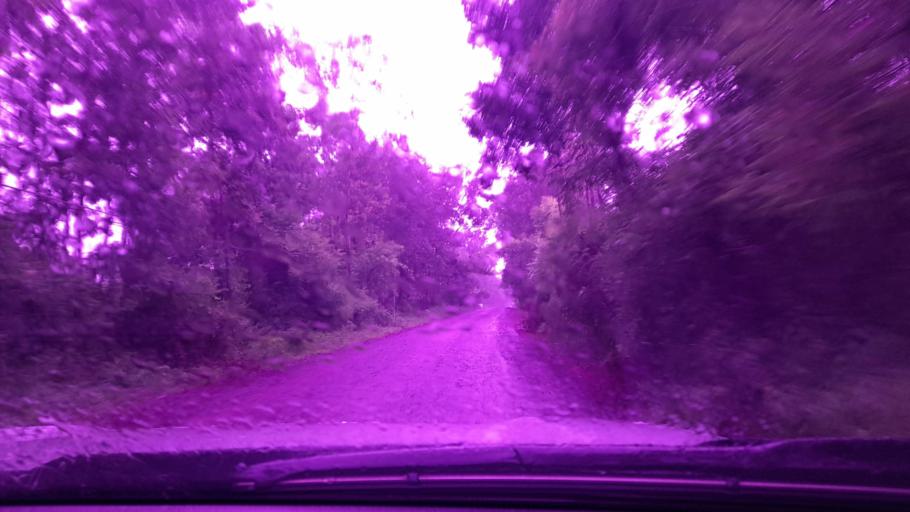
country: ET
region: Oromiya
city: Metu
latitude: 8.3172
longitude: 35.5986
